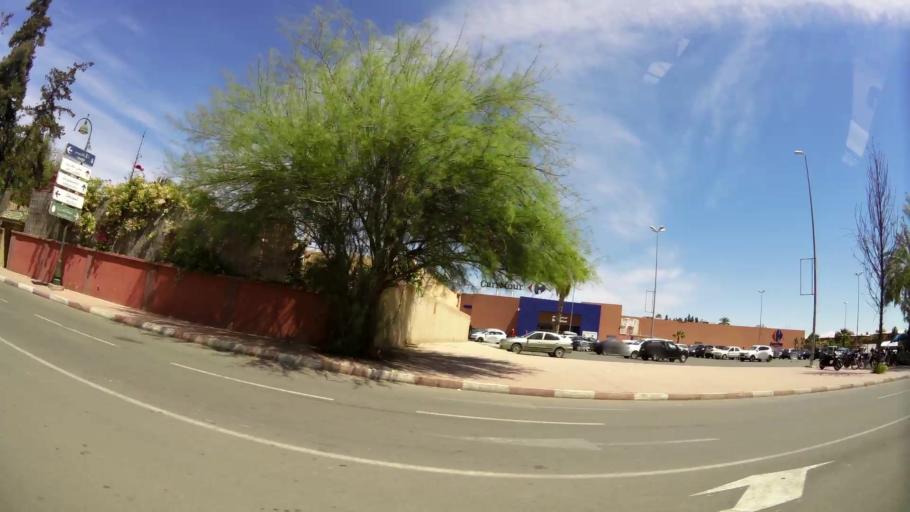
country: MA
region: Marrakech-Tensift-Al Haouz
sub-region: Marrakech
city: Marrakesh
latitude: 31.6509
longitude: -8.0605
